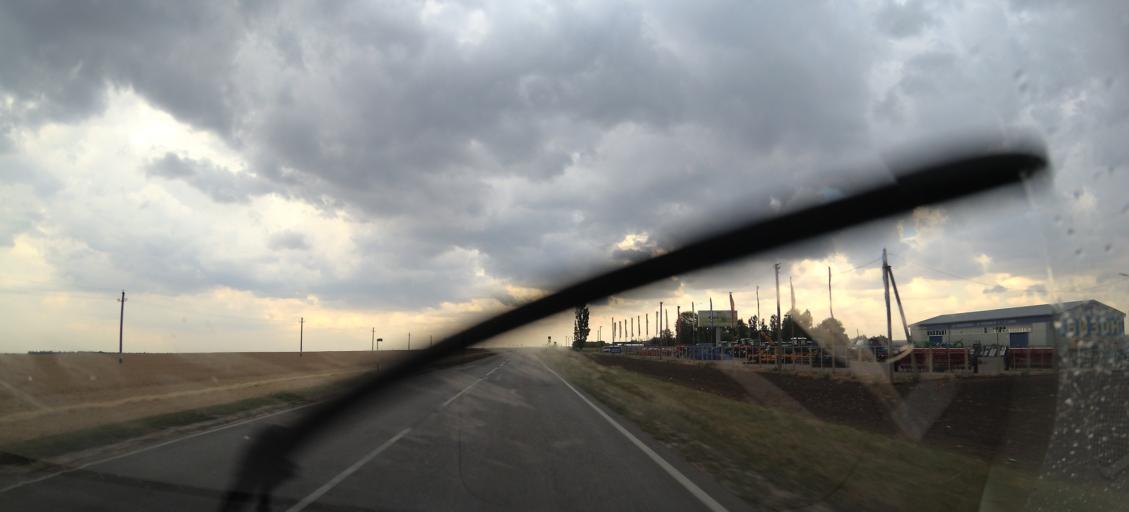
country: RU
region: Rostov
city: Orlovskiy
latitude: 46.8767
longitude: 41.9989
